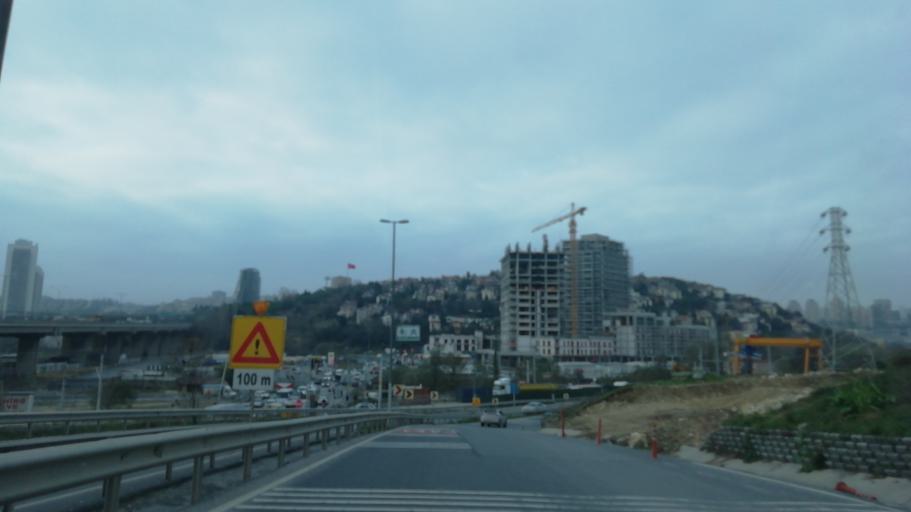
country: TR
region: Istanbul
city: Esenyurt
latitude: 41.0600
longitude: 28.7022
